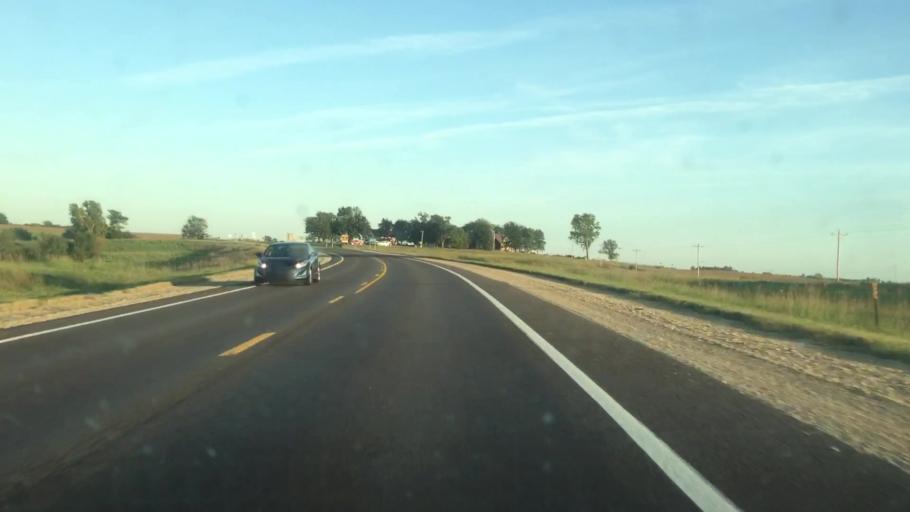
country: US
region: Kansas
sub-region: Atchison County
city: Atchison
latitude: 39.4343
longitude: -95.0890
